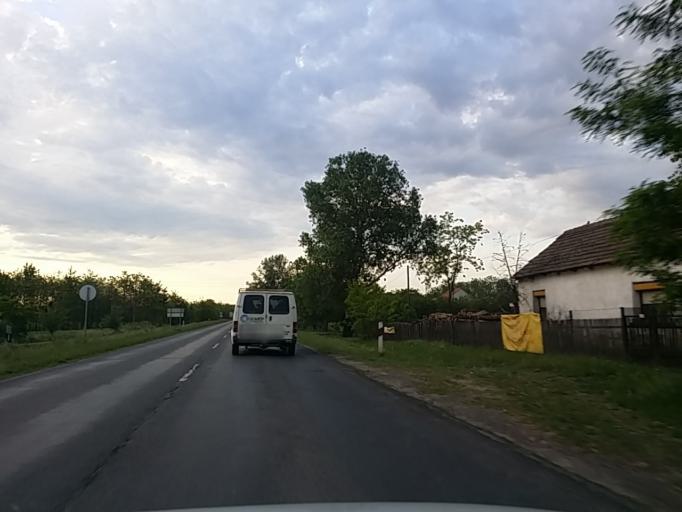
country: HU
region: Bacs-Kiskun
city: Lajosmizse
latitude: 47.0010
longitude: 19.5948
